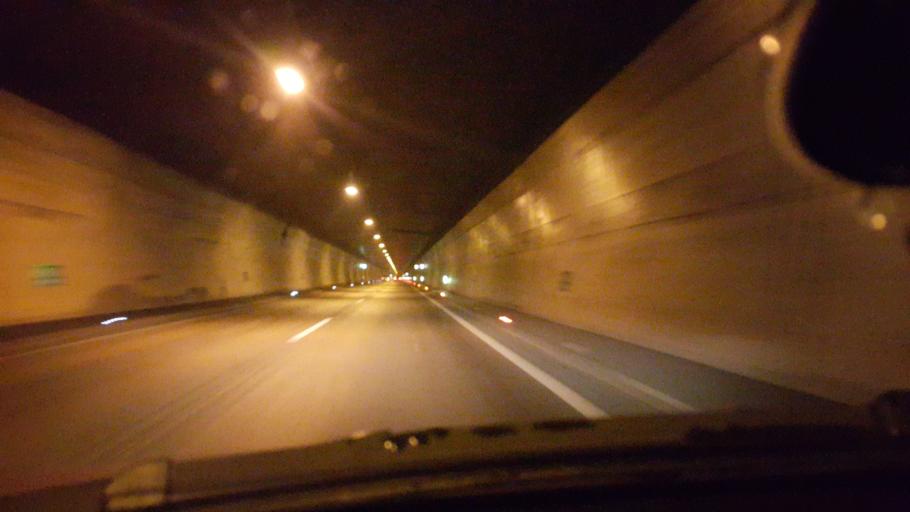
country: AT
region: Styria
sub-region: Graz Stadt
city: Goesting
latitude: 47.0820
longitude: 15.3882
